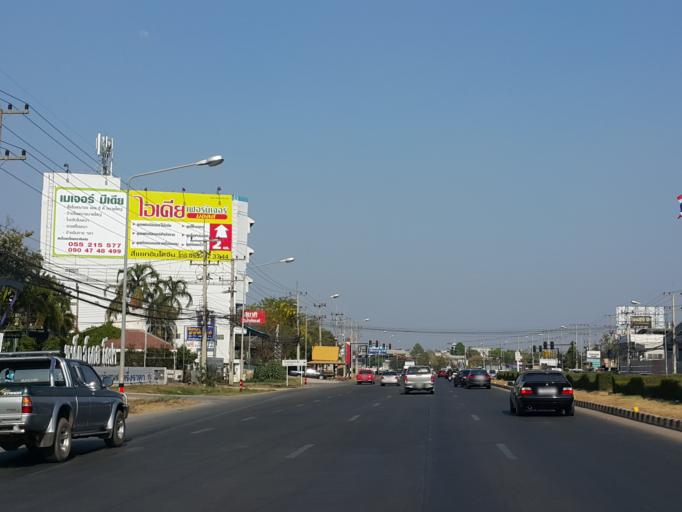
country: TH
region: Phitsanulok
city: Phitsanulok
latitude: 16.8170
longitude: 100.3013
